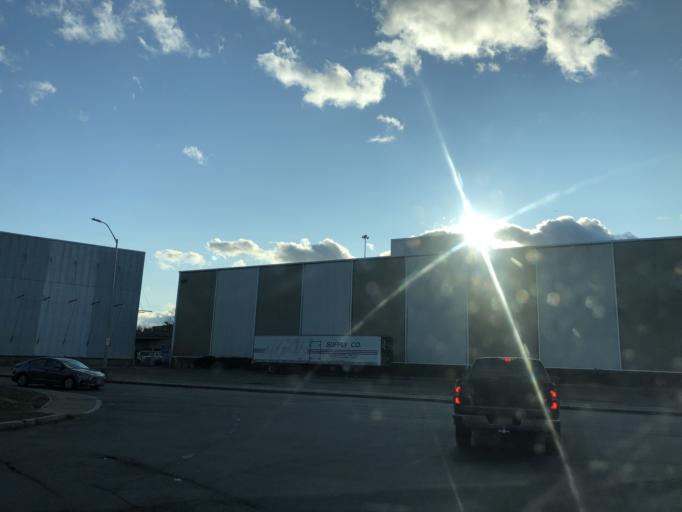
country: US
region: Massachusetts
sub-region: Bristol County
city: New Bedford
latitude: 41.6395
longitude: -70.9233
